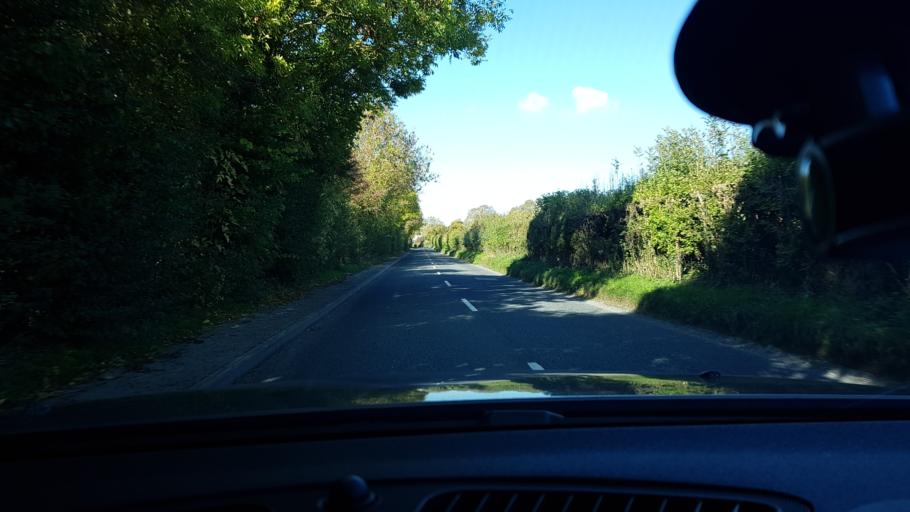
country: GB
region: England
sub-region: Wiltshire
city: Aldbourne
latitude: 51.4713
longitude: -1.6115
